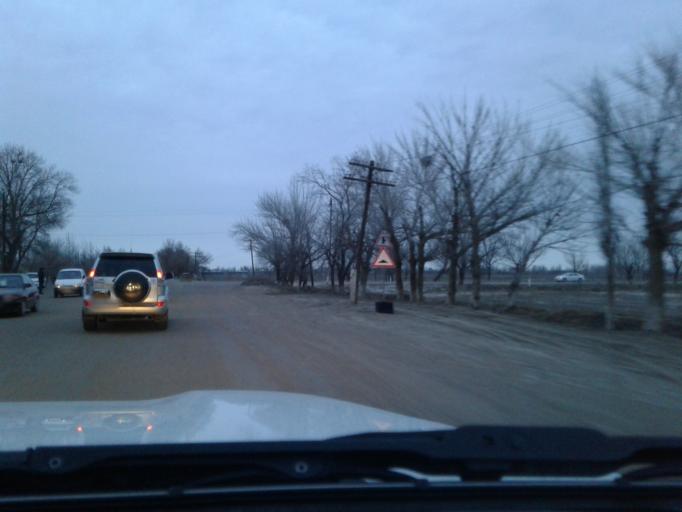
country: UZ
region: Karakalpakstan
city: Manghit
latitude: 42.0547
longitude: 59.9324
